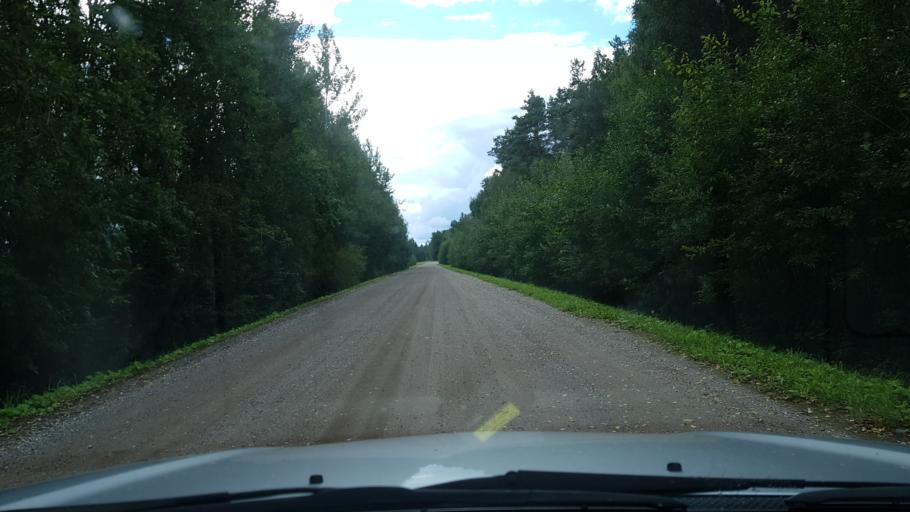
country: EE
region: Harju
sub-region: Rae vald
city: Vaida
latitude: 59.2678
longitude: 25.0481
